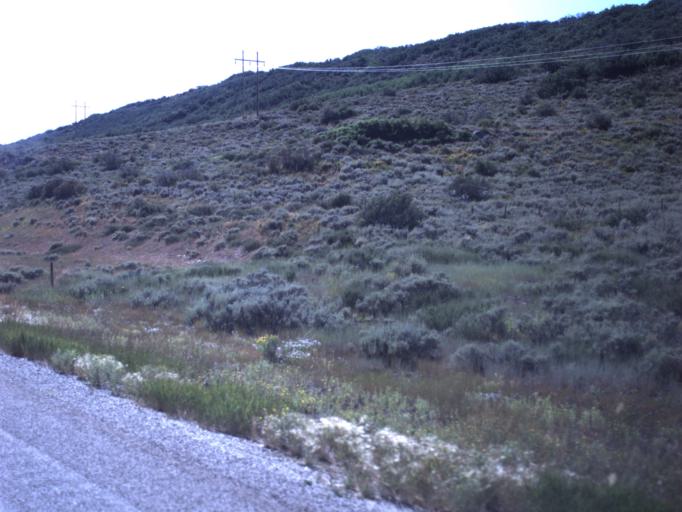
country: US
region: Utah
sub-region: Summit County
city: Francis
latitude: 40.1969
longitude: -111.0039
